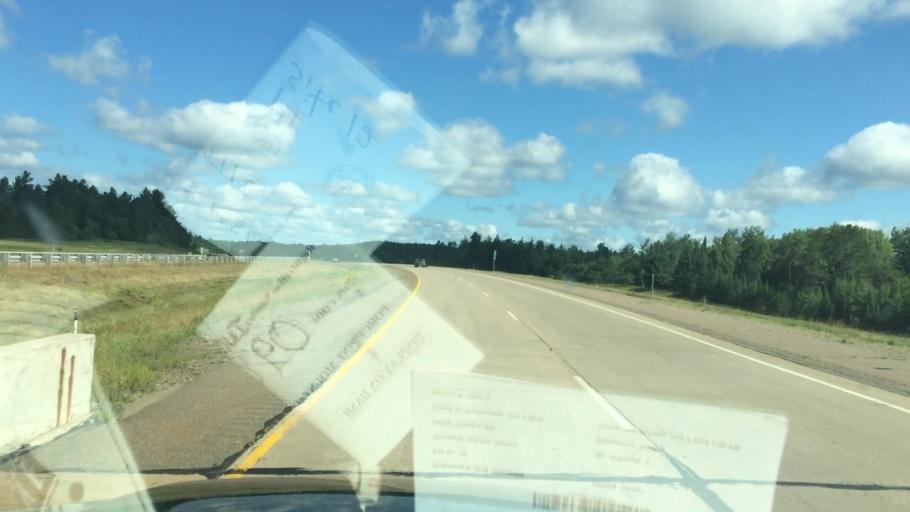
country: US
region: Wisconsin
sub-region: Lincoln County
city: Tomahawk
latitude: 45.4175
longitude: -89.6712
